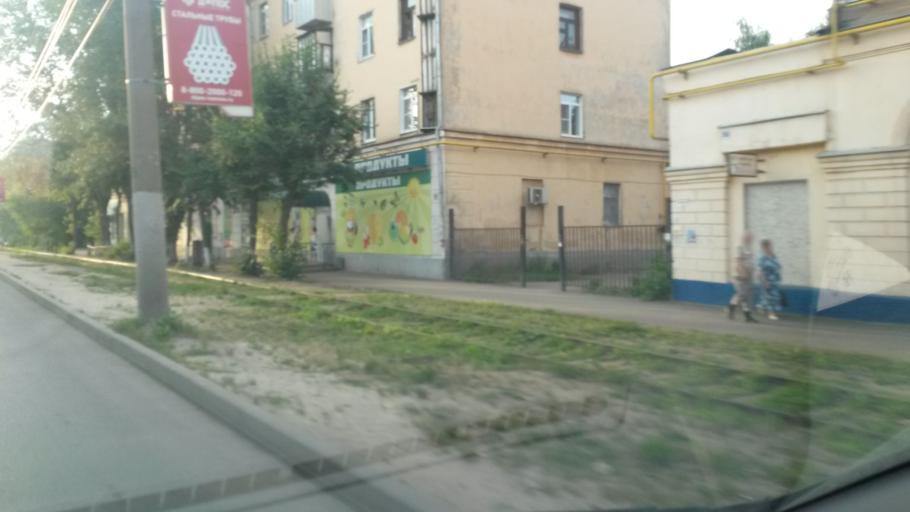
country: RU
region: Ivanovo
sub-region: Gorod Ivanovo
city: Ivanovo
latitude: 57.0077
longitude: 40.9484
